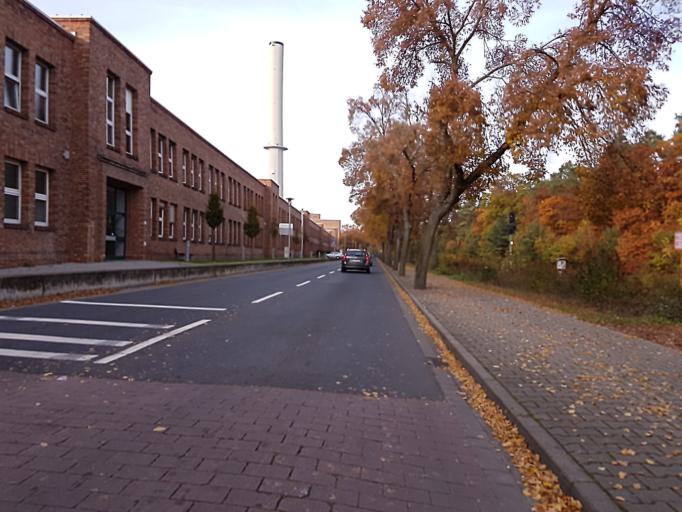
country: DE
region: Bavaria
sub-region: Regierungsbezirk Unterfranken
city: Elsenfeld
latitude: 49.8290
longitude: 9.1522
